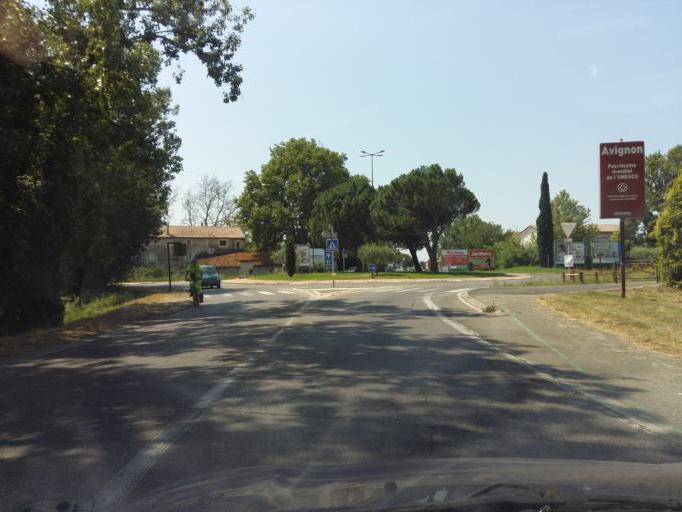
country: FR
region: Provence-Alpes-Cote d'Azur
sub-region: Departement du Vaucluse
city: Le Pontet
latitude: 43.9456
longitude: 4.8550
